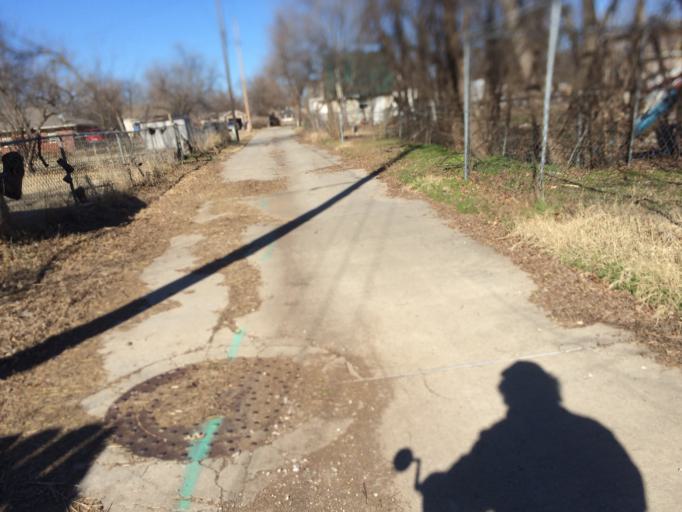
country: US
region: Oklahoma
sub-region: Cleveland County
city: Norman
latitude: 35.2213
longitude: -97.4312
